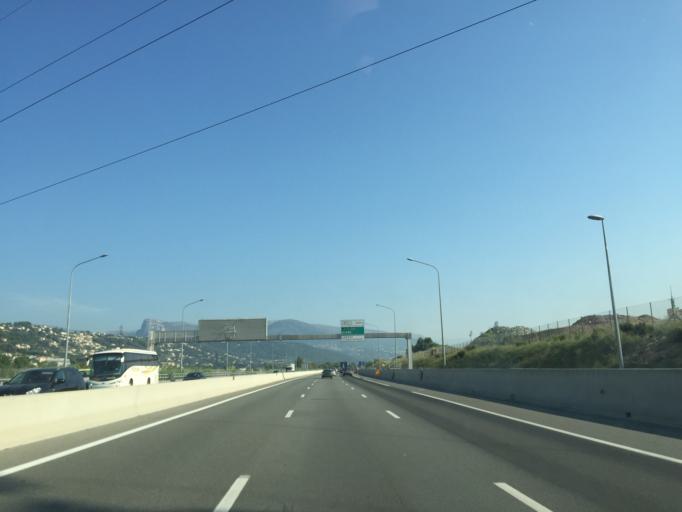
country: FR
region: Provence-Alpes-Cote d'Azur
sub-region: Departement des Alpes-Maritimes
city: Saint-Laurent-du-Var
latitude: 43.6853
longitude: 7.1915
